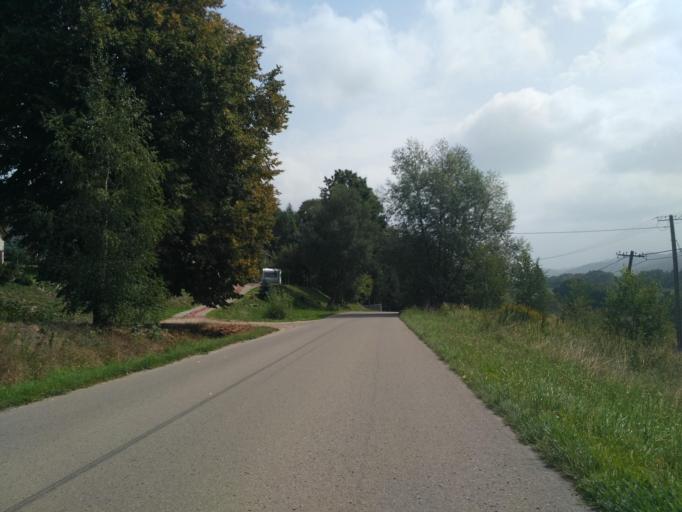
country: PL
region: Subcarpathian Voivodeship
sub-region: Powiat strzyzowski
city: Wisniowa
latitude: 49.8744
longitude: 21.6237
